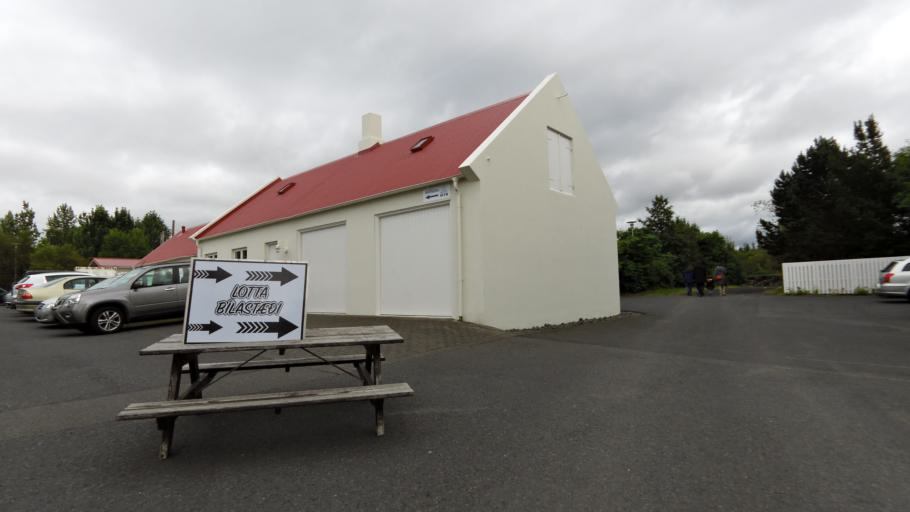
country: IS
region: Capital Region
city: Reykjavik
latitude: 64.1189
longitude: -21.8374
